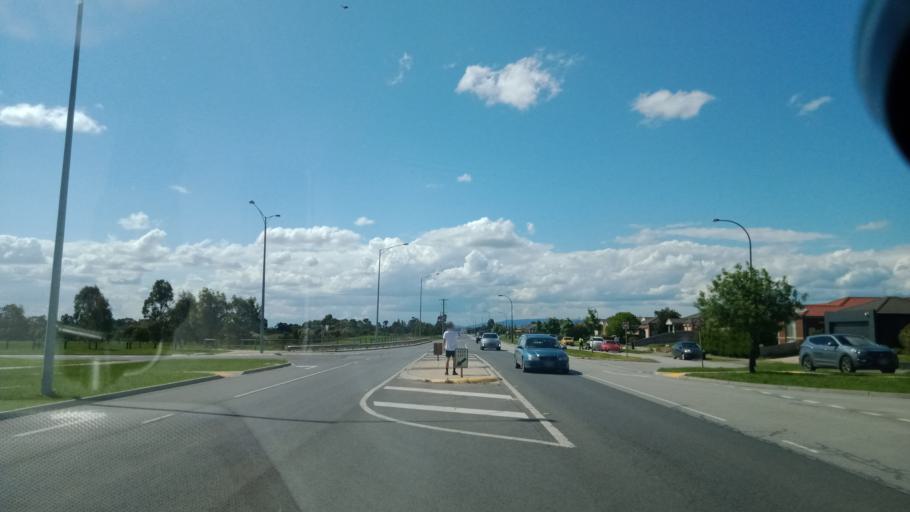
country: AU
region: Victoria
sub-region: Casey
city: Cranbourne West
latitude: -38.0917
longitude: 145.2558
